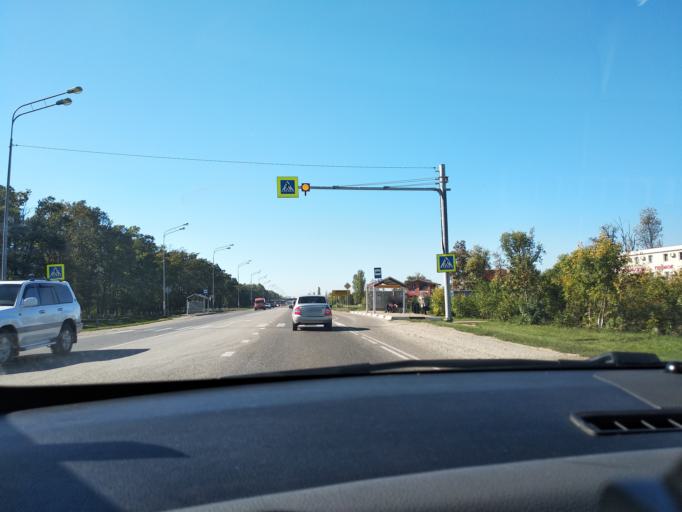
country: RU
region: Krasnodarskiy
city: Novotitarovskaya
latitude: 45.1401
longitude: 39.0378
